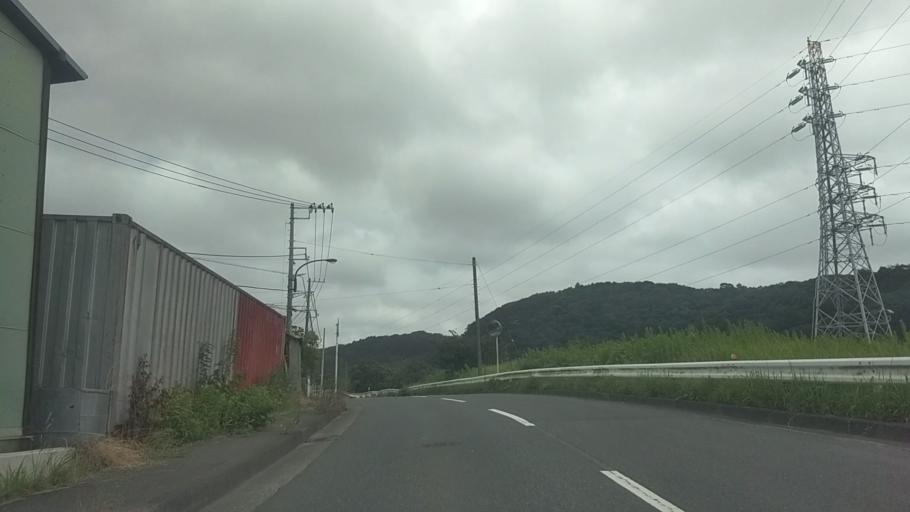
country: JP
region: Kanagawa
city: Yokosuka
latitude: 35.2300
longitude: 139.6313
